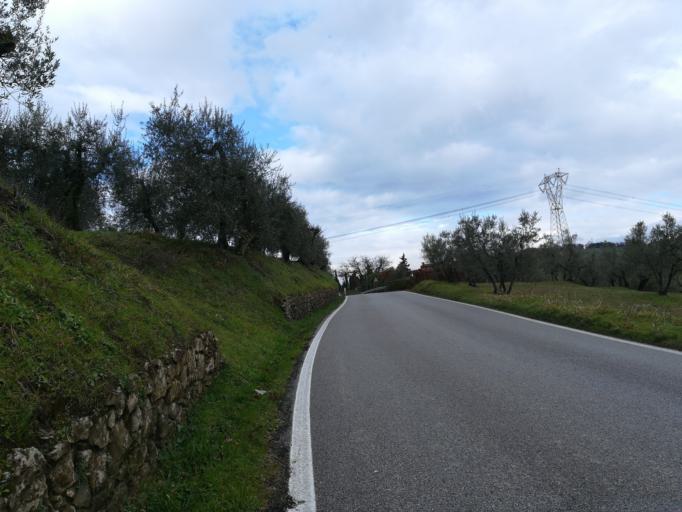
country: IT
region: Tuscany
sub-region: Provincia di Prato
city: Carmignano
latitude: 43.7989
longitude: 11.0316
